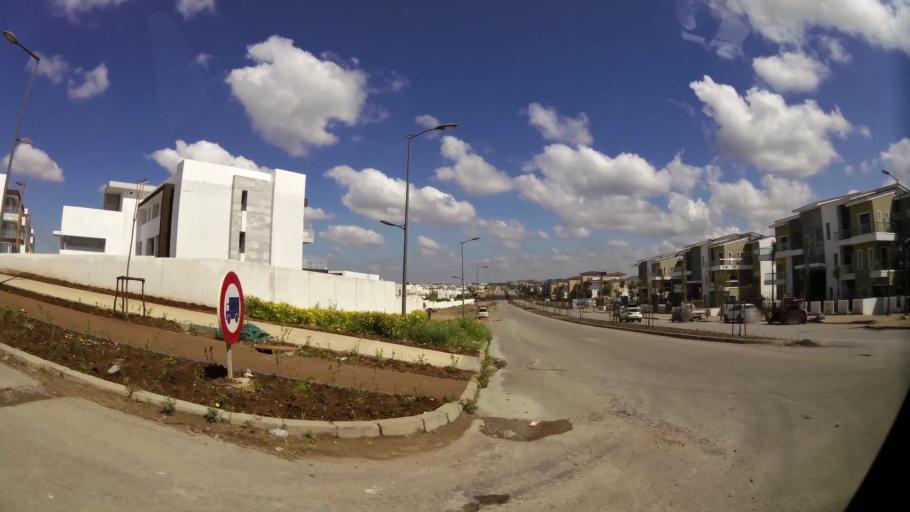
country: MA
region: Grand Casablanca
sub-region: Nouaceur
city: Bouskoura
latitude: 33.4885
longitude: -7.6052
